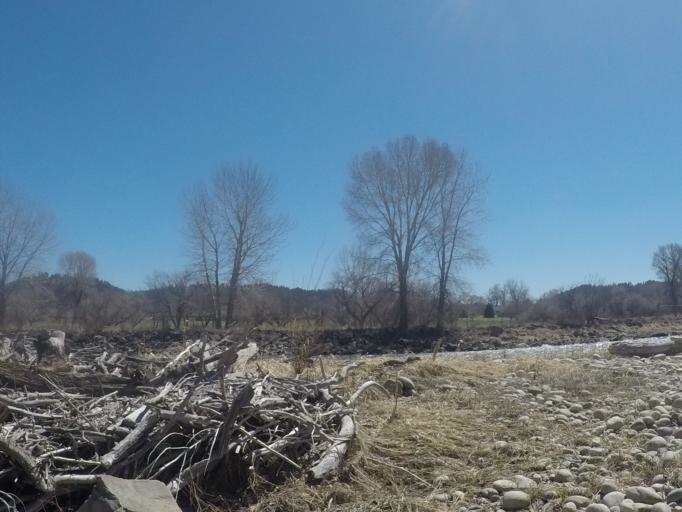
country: US
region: Montana
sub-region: Stillwater County
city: Columbus
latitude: 45.6189
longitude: -109.2914
